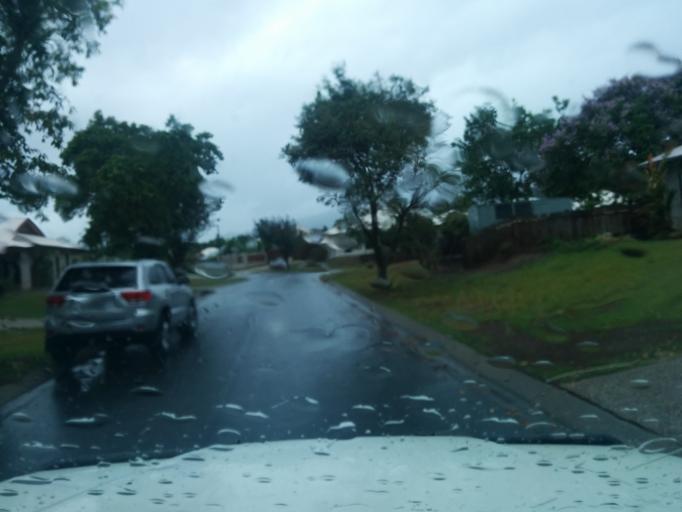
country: AU
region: Queensland
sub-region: Cairns
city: Woree
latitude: -16.9850
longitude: 145.7378
